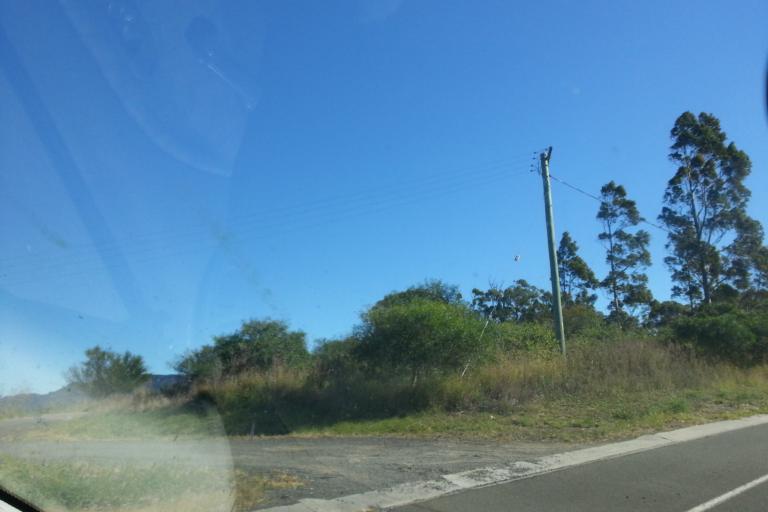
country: AU
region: New South Wales
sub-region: Wollongong
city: Dapto
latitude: -34.5194
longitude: 150.7843
